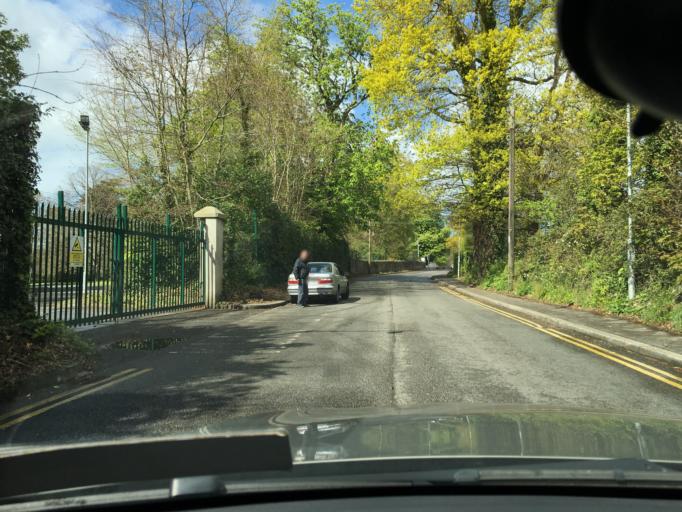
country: IE
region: Leinster
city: Castleknock
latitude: 53.3668
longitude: -6.3619
